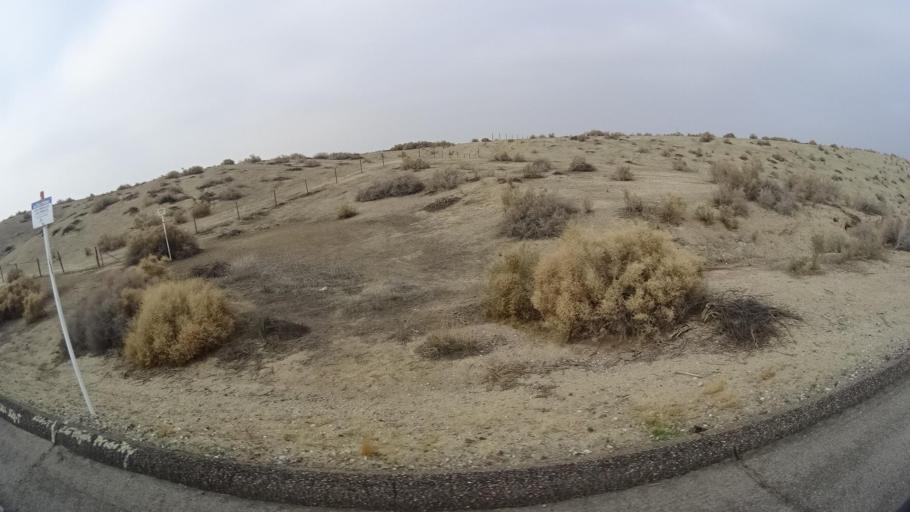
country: US
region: California
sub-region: Kern County
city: Ford City
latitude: 35.1594
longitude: -119.3405
